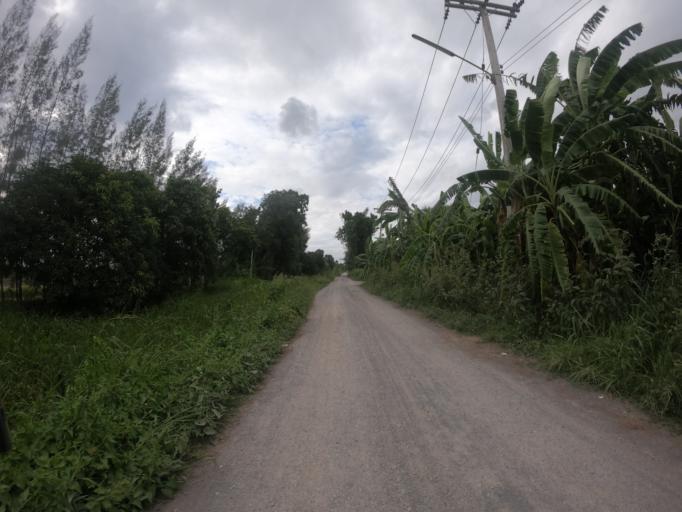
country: TH
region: Pathum Thani
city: Nong Suea
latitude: 14.0758
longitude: 100.8352
